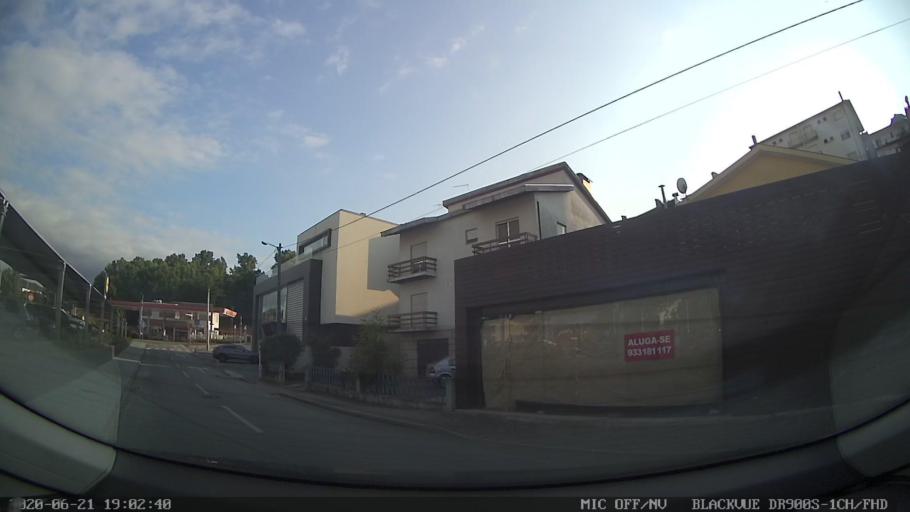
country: PT
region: Porto
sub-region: Amarante
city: Amarante
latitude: 41.2737
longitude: -8.0899
